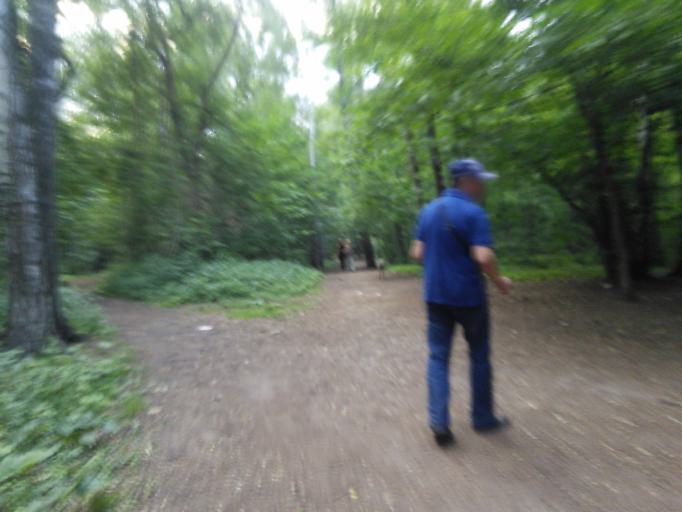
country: RU
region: Moscow
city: Sokol'niki
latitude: 55.8129
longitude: 37.6669
